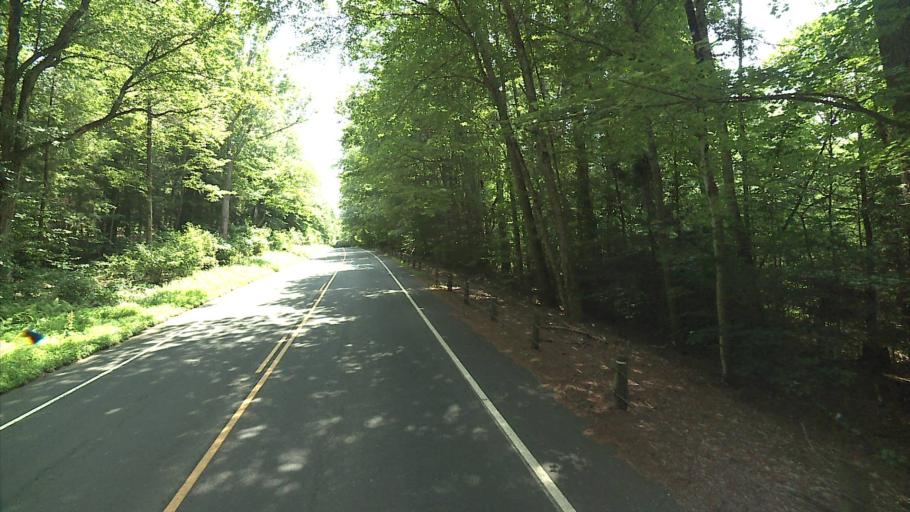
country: US
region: Massachusetts
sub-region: Hampden County
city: Granville
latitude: 42.0208
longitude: -72.9271
